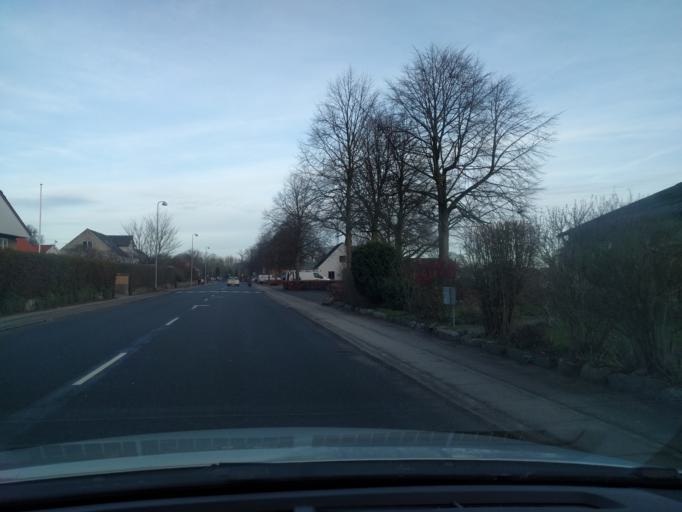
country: DK
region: South Denmark
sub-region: Odense Kommune
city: Neder Holluf
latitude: 55.3553
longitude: 10.4914
